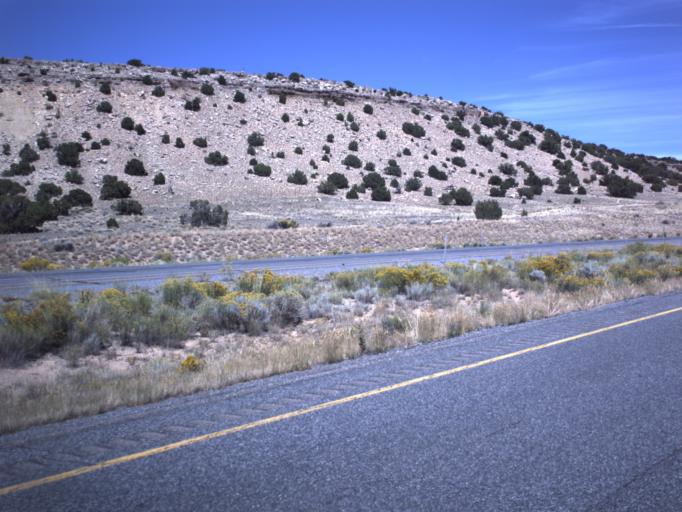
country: US
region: Utah
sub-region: Emery County
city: Castle Dale
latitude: 38.9051
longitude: -110.5522
